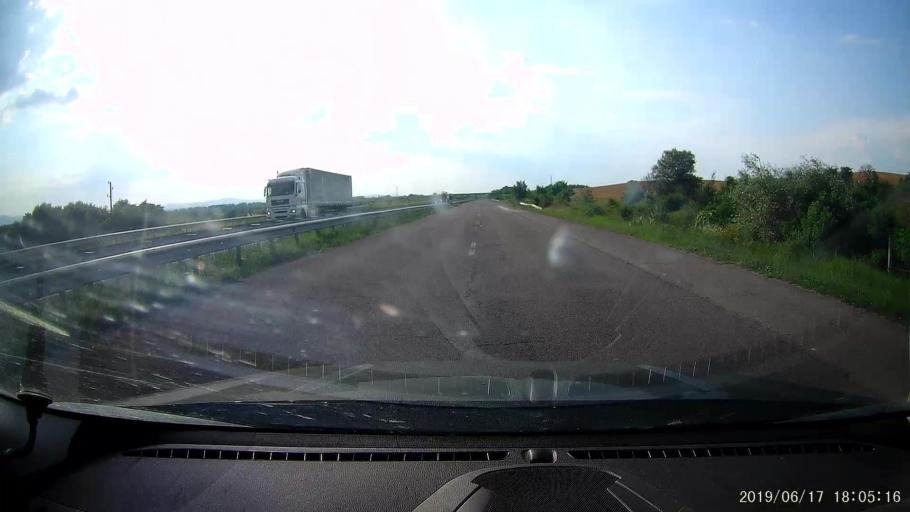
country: BG
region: Khaskovo
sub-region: Obshtina Svilengrad
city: Svilengrad
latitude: 41.7961
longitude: 26.1796
